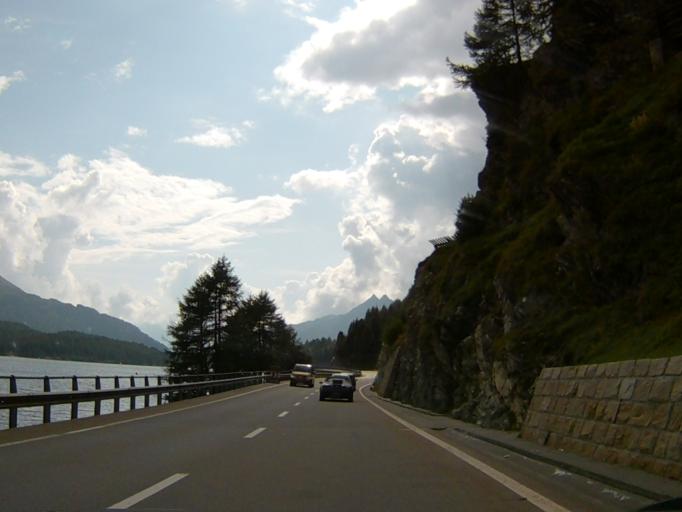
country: CH
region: Grisons
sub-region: Maloja District
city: Silvaplana
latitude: 46.4166
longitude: 9.7208
